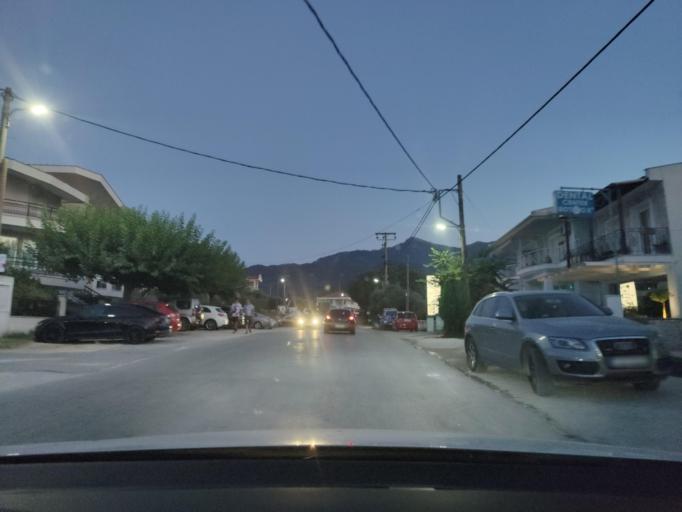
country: GR
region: East Macedonia and Thrace
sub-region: Nomos Kavalas
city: Thasos
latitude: 40.7770
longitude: 24.7001
